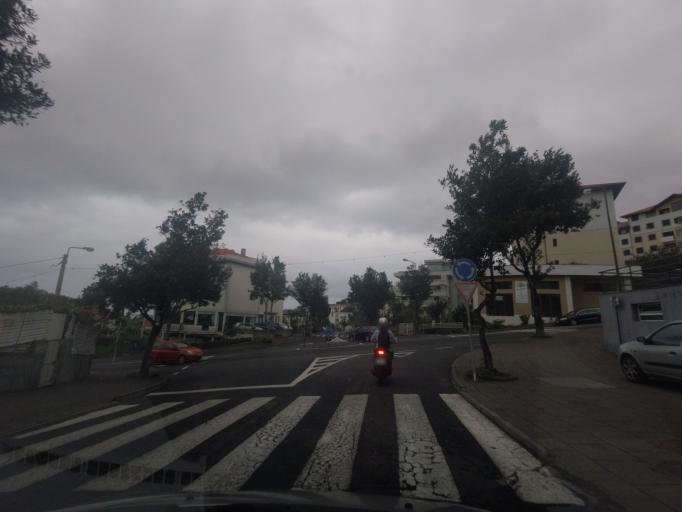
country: PT
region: Madeira
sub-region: Funchal
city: Funchal
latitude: 32.6476
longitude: -16.9302
